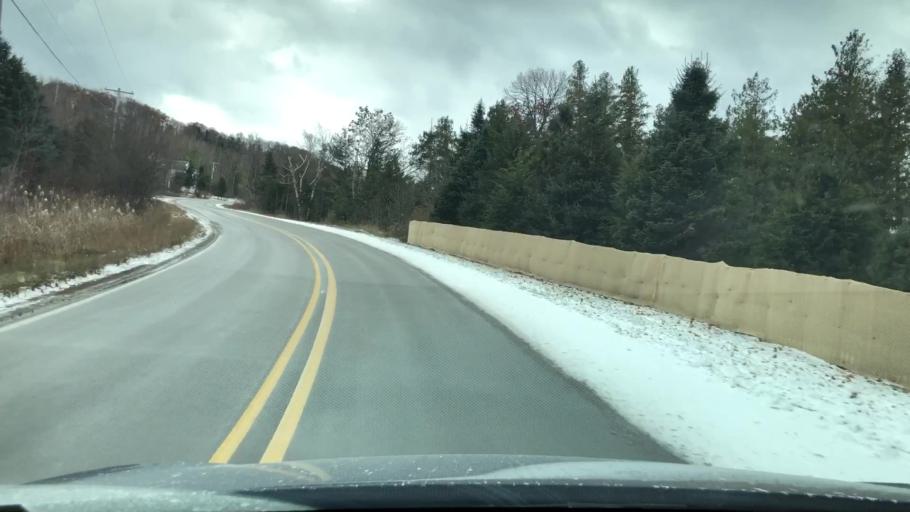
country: US
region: Michigan
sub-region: Leelanau County
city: Greilickville
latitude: 44.8378
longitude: -85.5618
